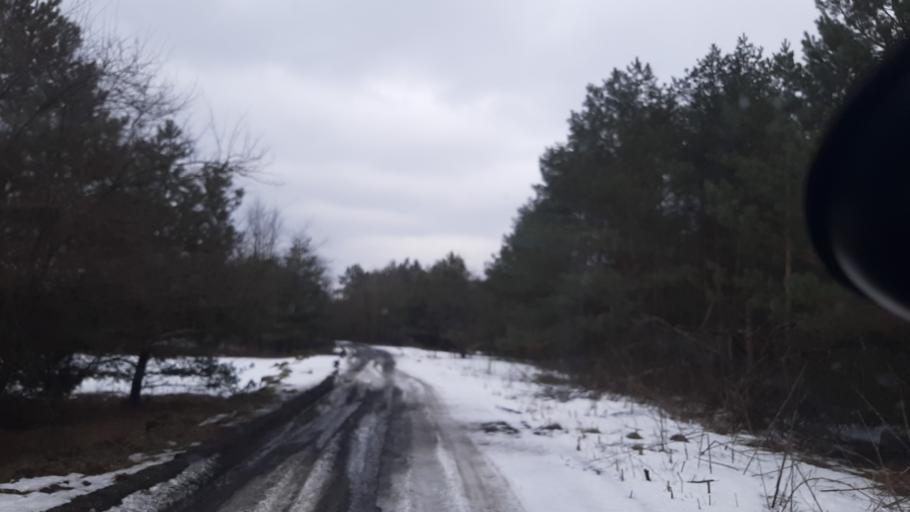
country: PL
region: Lublin Voivodeship
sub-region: Powiat wlodawski
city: Wlodawa
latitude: 51.5160
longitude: 23.6016
